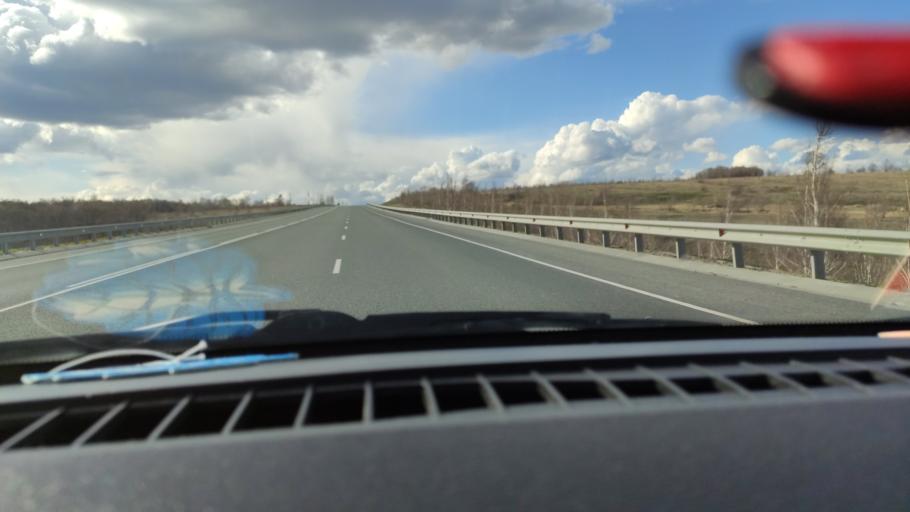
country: RU
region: Saratov
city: Shikhany
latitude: 52.1419
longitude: 47.2055
